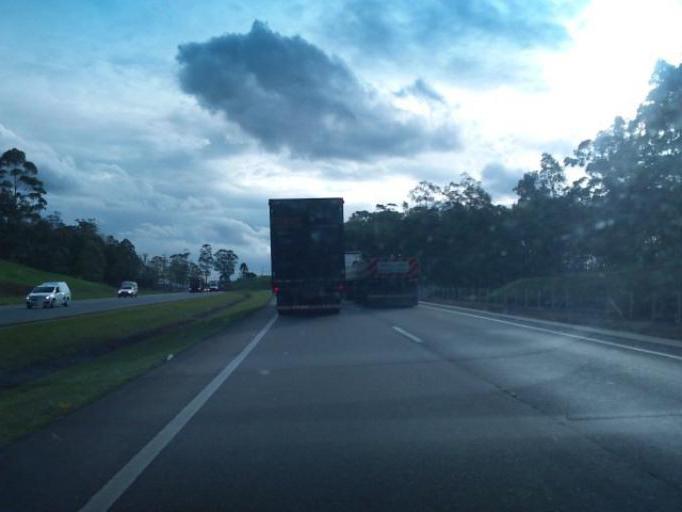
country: BR
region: Parana
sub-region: Piraquara
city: Piraquara
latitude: -25.4341
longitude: -49.0886
